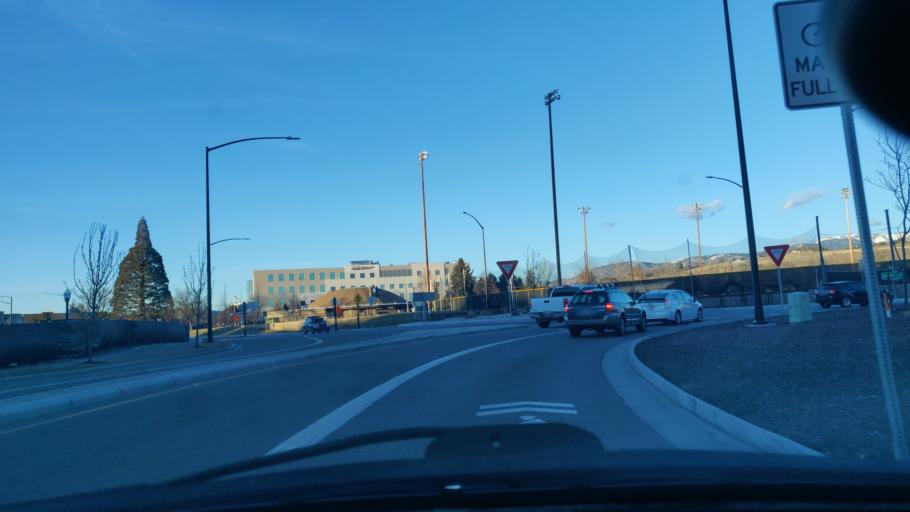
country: US
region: Idaho
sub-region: Ada County
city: Boise
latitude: 43.6131
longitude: -116.1907
